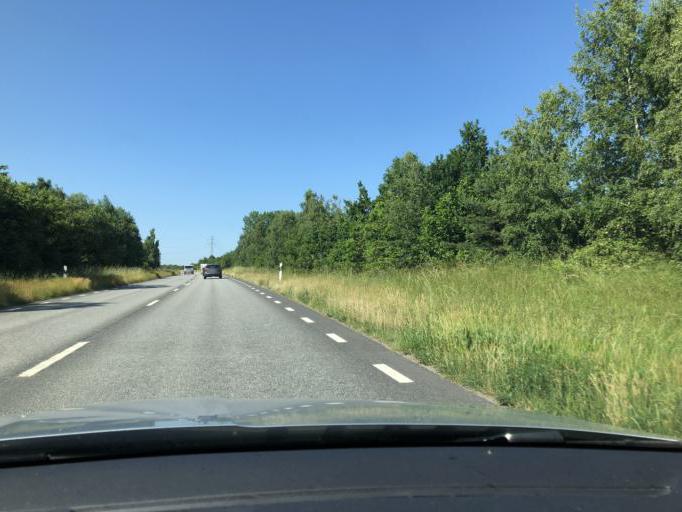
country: SE
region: Skane
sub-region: Bromolla Kommun
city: Bromoella
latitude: 56.0735
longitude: 14.4990
